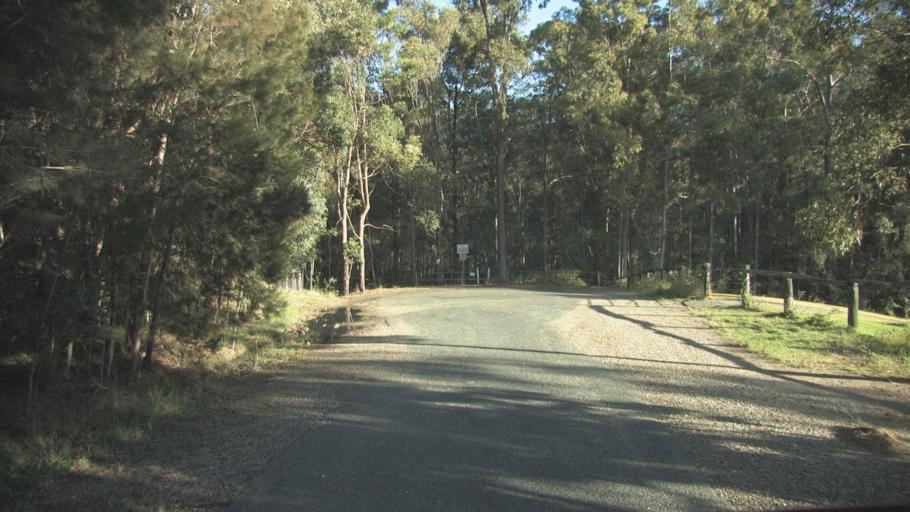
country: AU
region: Queensland
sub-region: Logan
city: Windaroo
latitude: -27.7461
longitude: 153.1482
